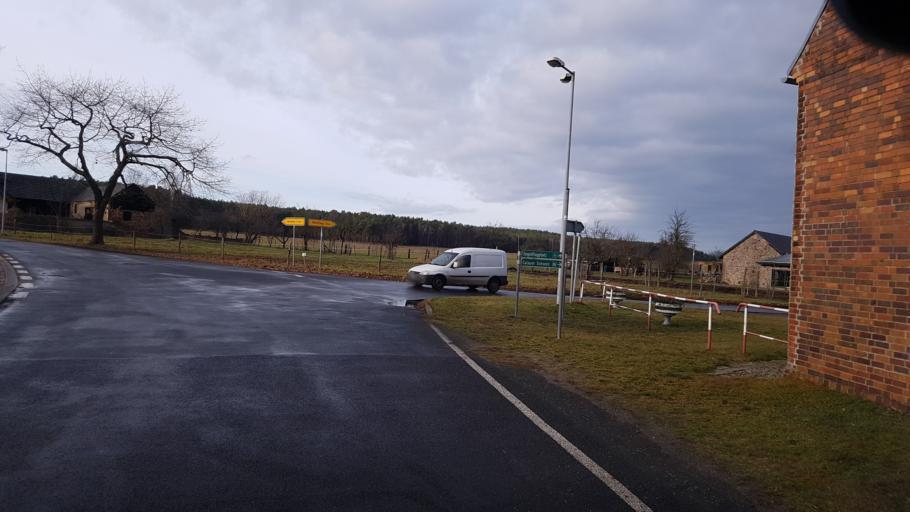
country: DE
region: Brandenburg
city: Altdobern
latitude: 51.6708
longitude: 13.9832
